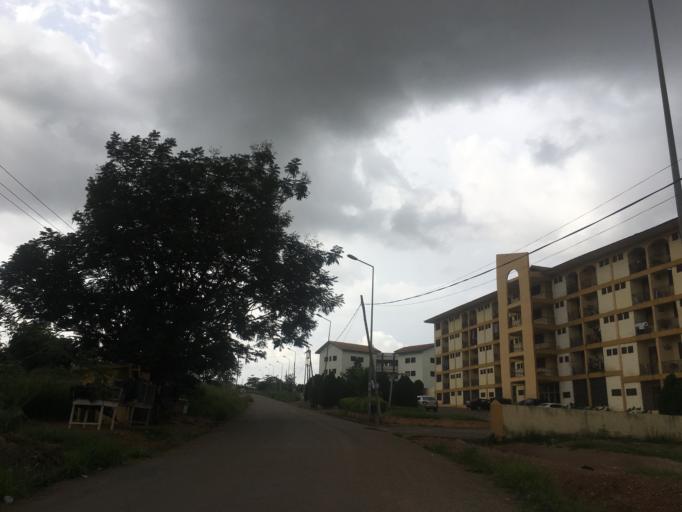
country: GH
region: Ashanti
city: Mamponteng
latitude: 6.6864
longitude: -1.5571
